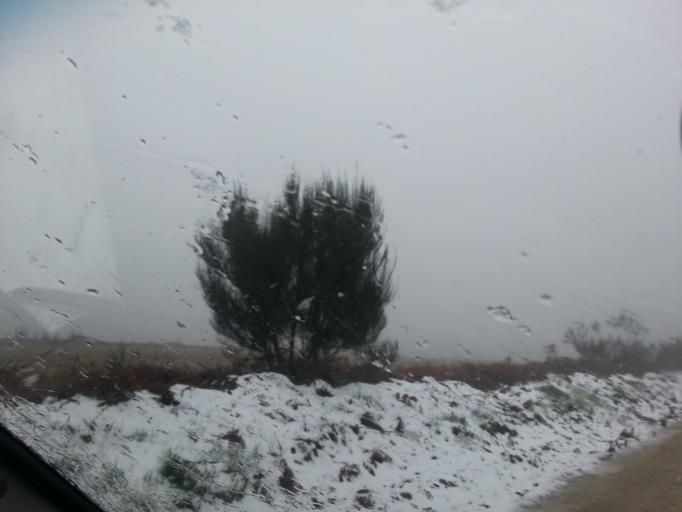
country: PT
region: Guarda
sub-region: Celorico da Beira
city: Celorico da Beira
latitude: 40.5288
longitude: -7.4464
